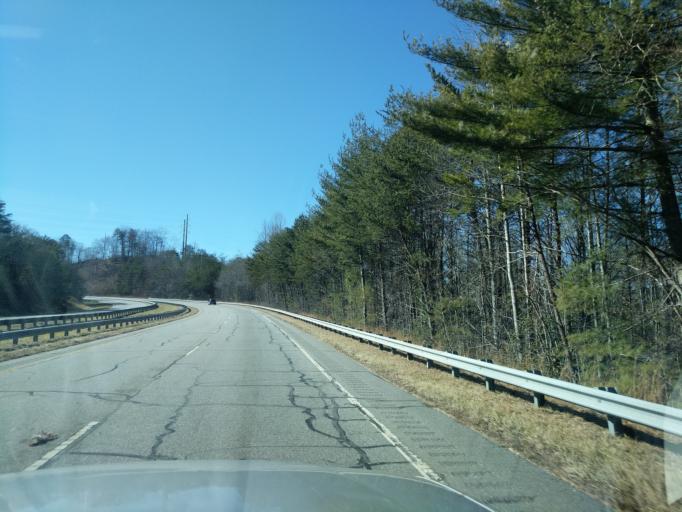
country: US
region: North Carolina
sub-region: Swain County
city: Bryson City
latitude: 35.4129
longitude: -83.4511
